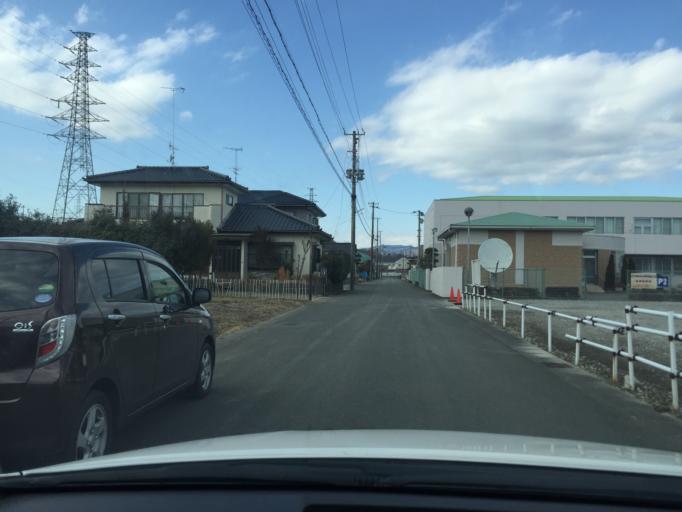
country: JP
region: Fukushima
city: Iwaki
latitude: 36.9458
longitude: 140.8554
